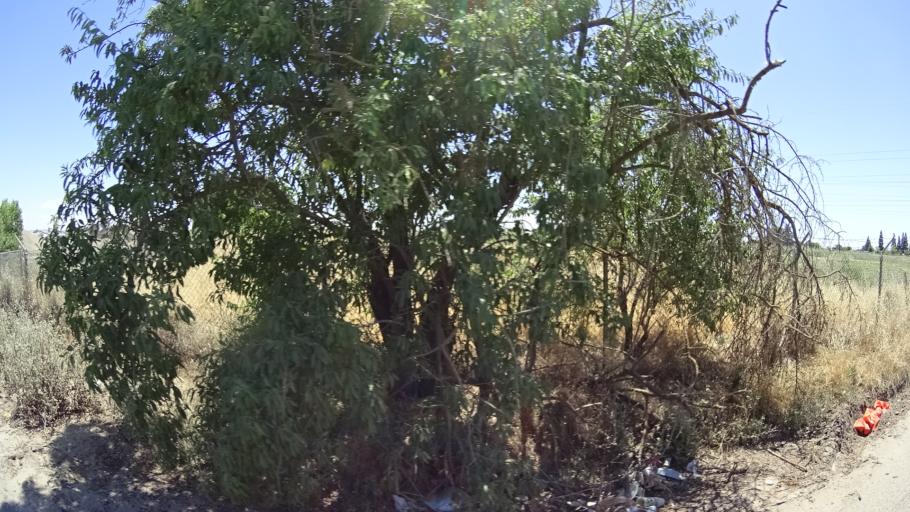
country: US
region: California
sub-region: Sacramento County
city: Rosemont
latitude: 38.5471
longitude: -121.3866
